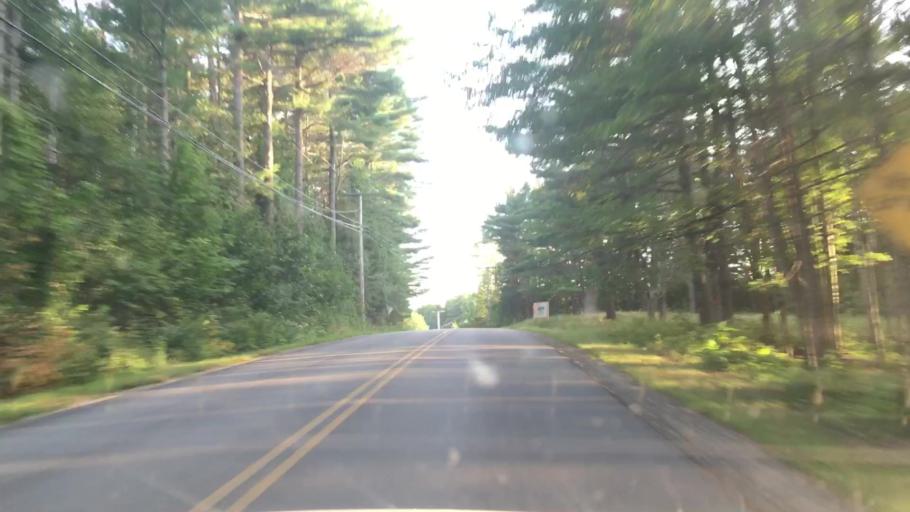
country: US
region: Maine
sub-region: Penobscot County
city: Hampden
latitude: 44.7109
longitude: -68.8872
